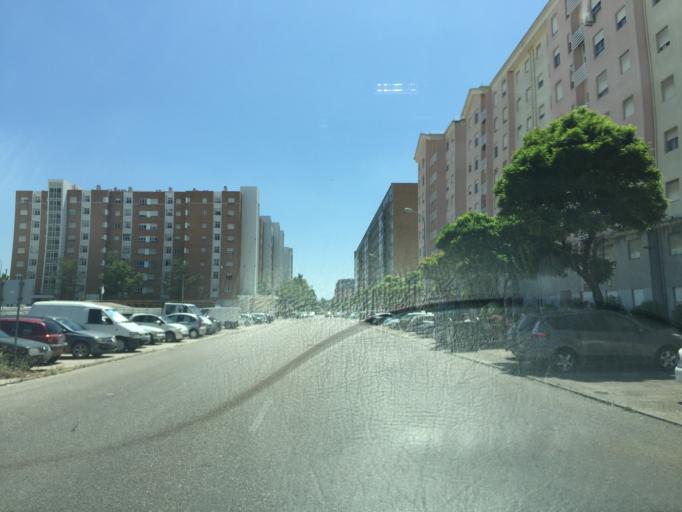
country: PT
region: Lisbon
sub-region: Odivelas
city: Olival do Basto
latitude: 38.7811
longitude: -9.1480
